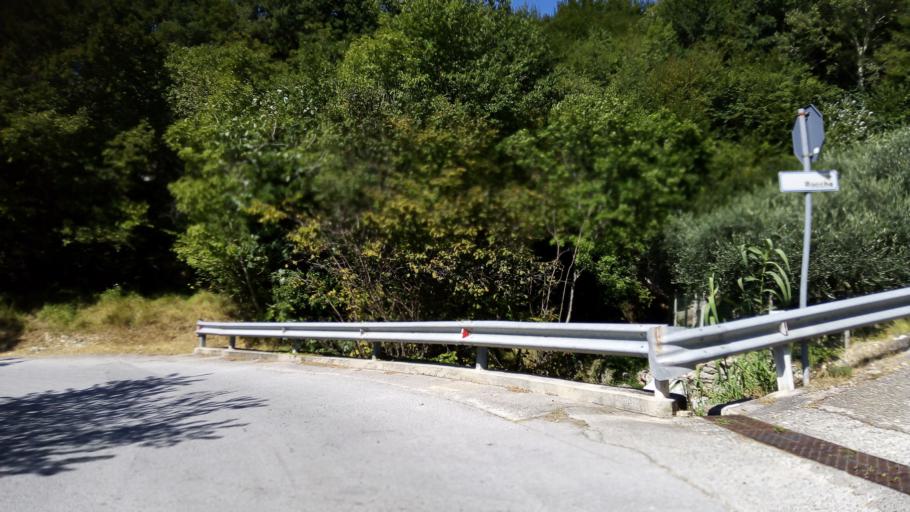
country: IT
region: Liguria
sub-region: Provincia di Savona
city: Balestrino
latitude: 44.1450
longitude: 8.1653
